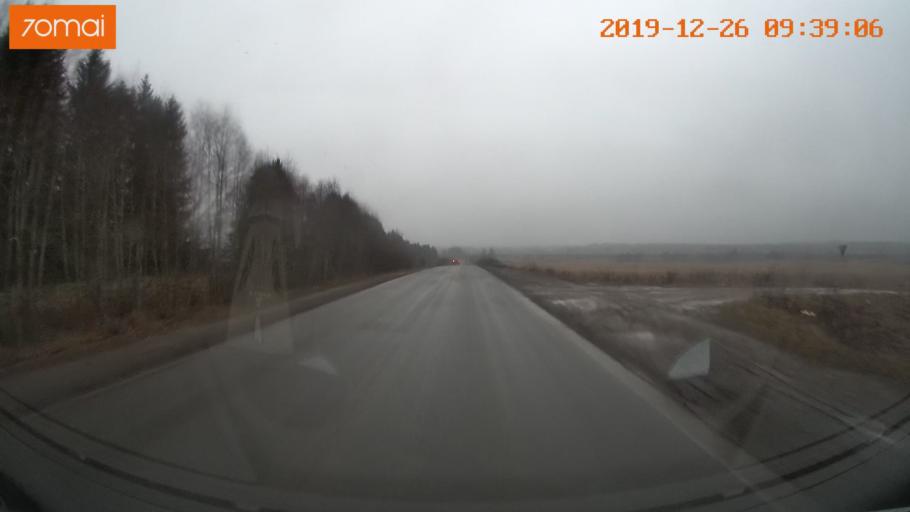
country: RU
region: Vologda
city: Vologda
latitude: 59.1510
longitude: 40.0310
